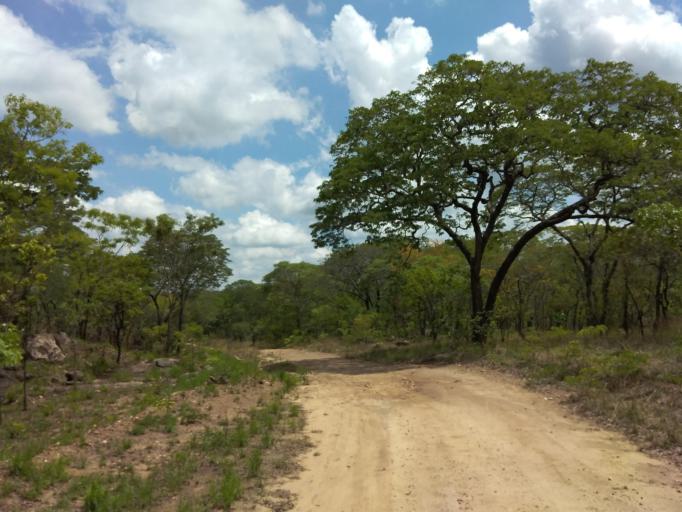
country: ZM
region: Central
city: Mkushi
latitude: -14.0676
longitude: 29.9598
